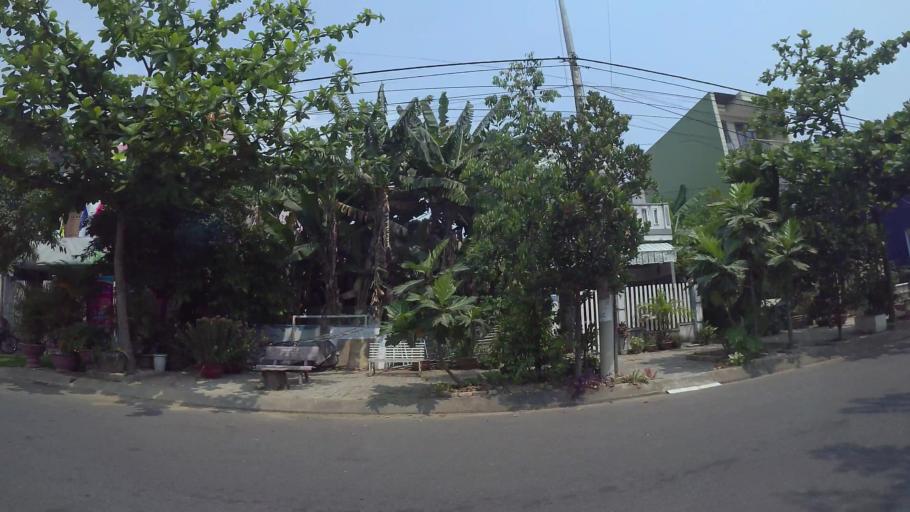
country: VN
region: Da Nang
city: Cam Le
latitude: 16.0001
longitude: 108.2173
